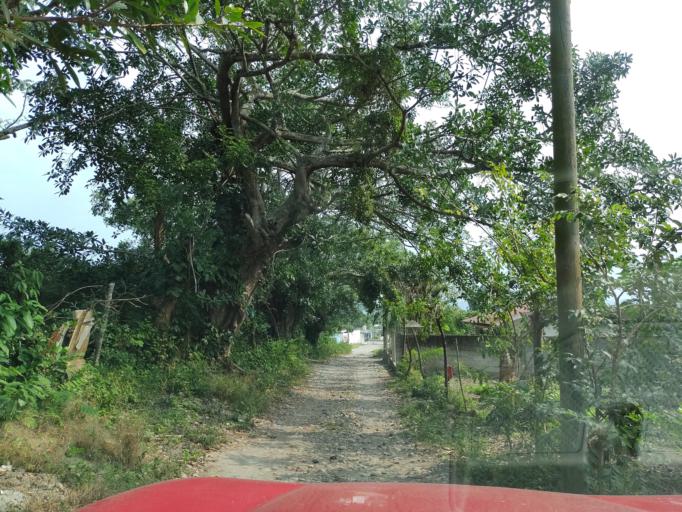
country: MX
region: Veracruz
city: Agua Dulce
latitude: 20.3608
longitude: -97.2960
